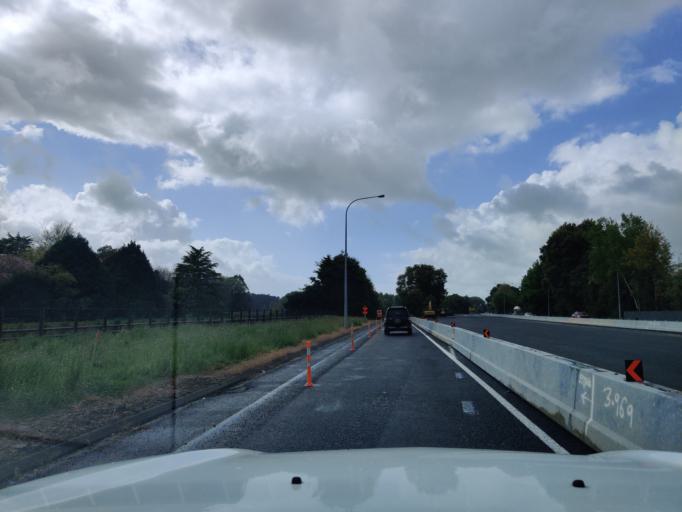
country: NZ
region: Waikato
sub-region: Hamilton City
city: Hamilton
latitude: -37.8258
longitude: 175.3545
